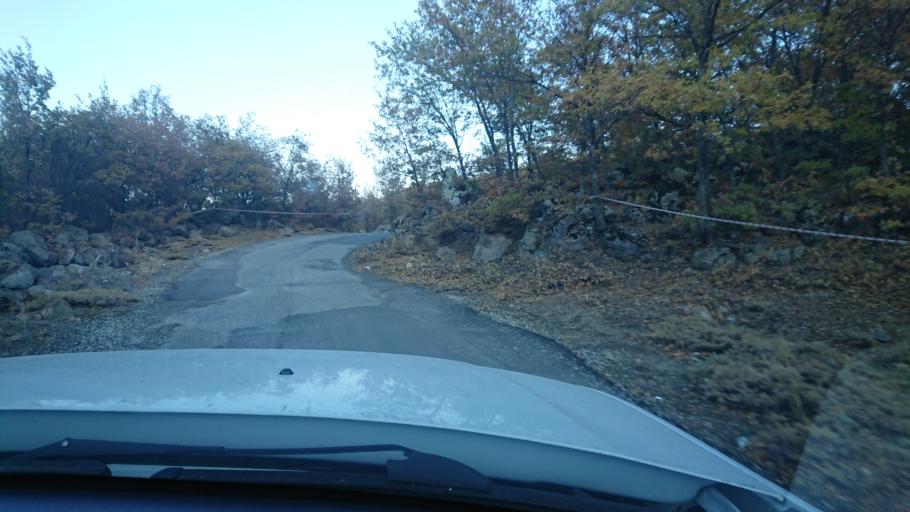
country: TR
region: Aksaray
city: Taspinar
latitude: 38.1672
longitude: 34.1934
